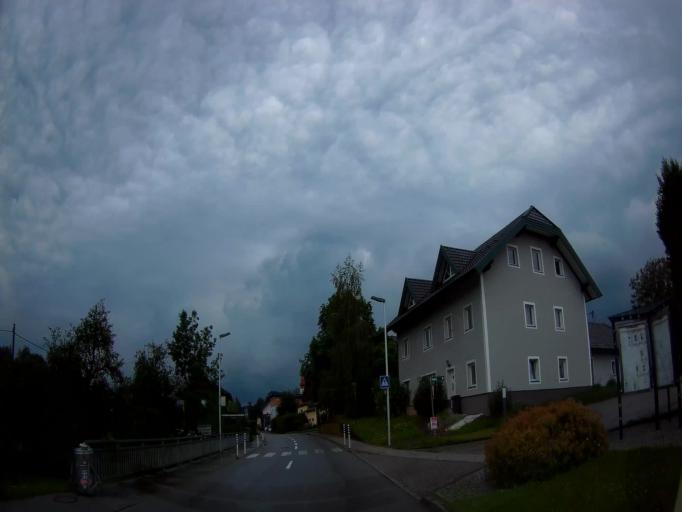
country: AT
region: Salzburg
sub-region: Politischer Bezirk Salzburg-Umgebung
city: Mattsee
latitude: 48.0502
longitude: 13.1482
